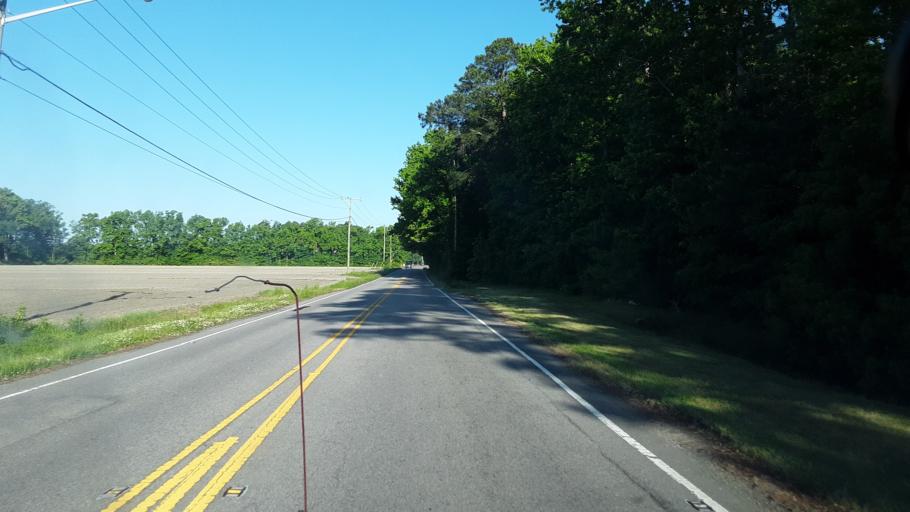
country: US
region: Virginia
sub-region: City of Virginia Beach
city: Virginia Beach
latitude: 36.7224
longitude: -76.0537
